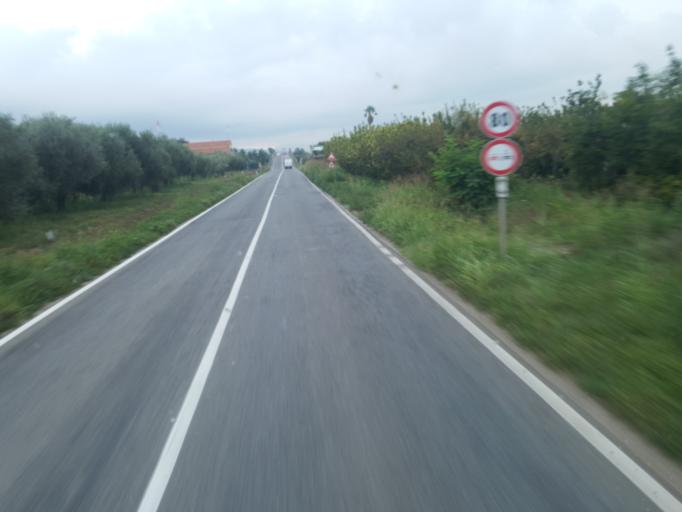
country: IT
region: Campania
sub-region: Provincia di Caserta
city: Sparanise
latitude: 41.1742
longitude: 14.1292
